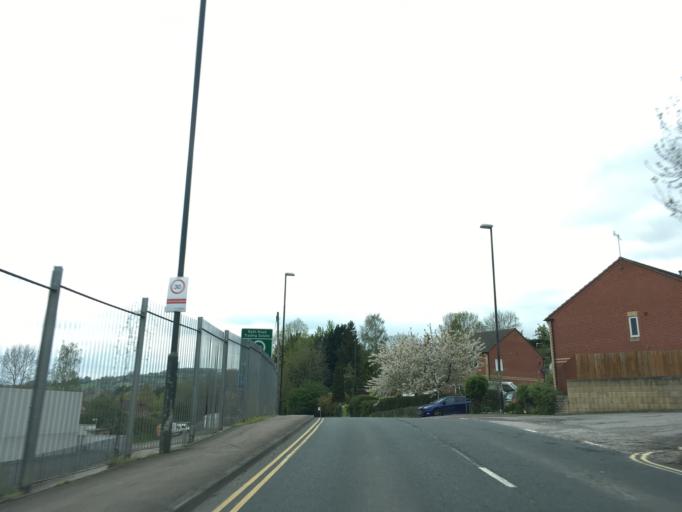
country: GB
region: England
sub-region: Gloucestershire
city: Stroud
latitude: 51.7372
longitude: -2.2350
